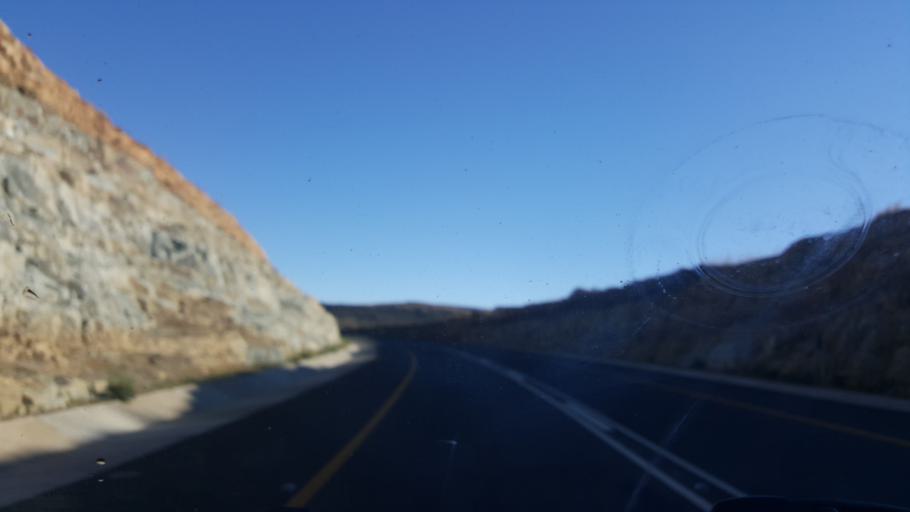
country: ZA
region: Eastern Cape
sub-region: Chris Hani District Municipality
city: Middelburg
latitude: -31.3788
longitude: 25.0344
